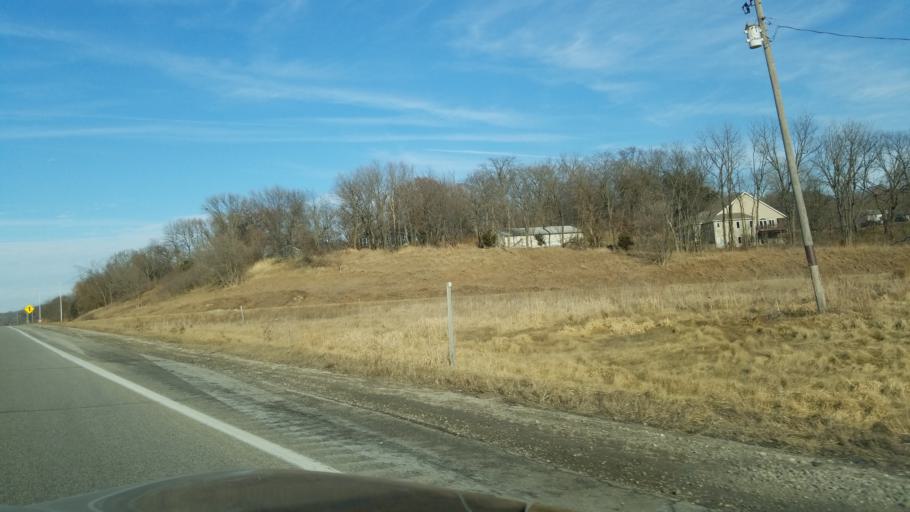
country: US
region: Iowa
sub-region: Linn County
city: Ely
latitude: 41.9271
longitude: -91.5422
